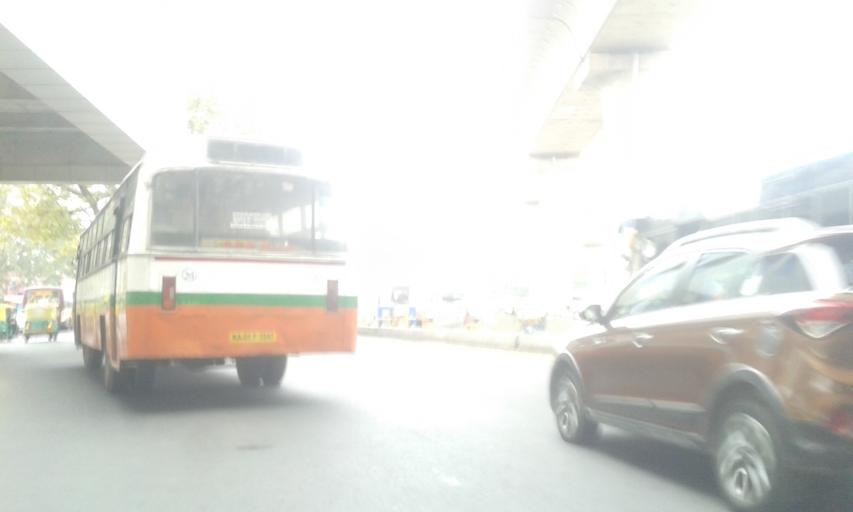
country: IN
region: Karnataka
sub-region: Bangalore Urban
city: Bangalore
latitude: 12.9161
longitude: 77.5737
